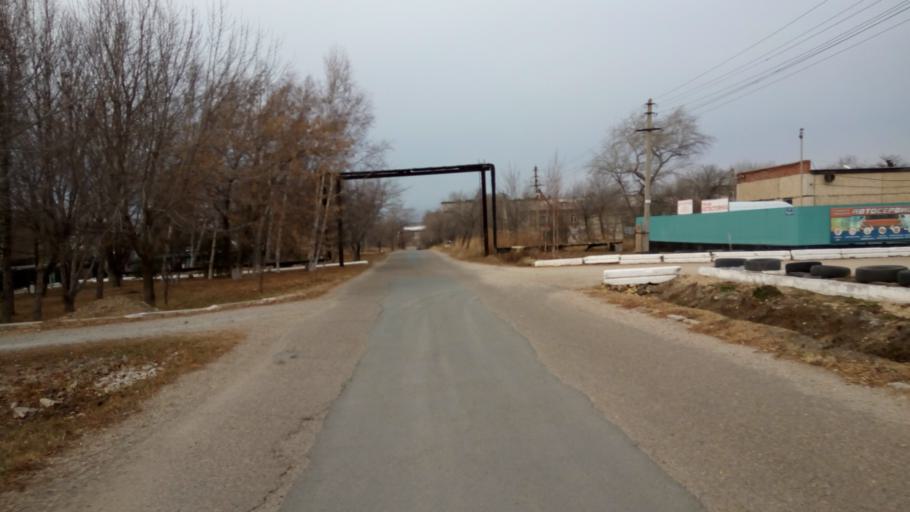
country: RU
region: Primorskiy
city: Novoshakhtinskiy
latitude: 44.0234
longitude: 132.1623
